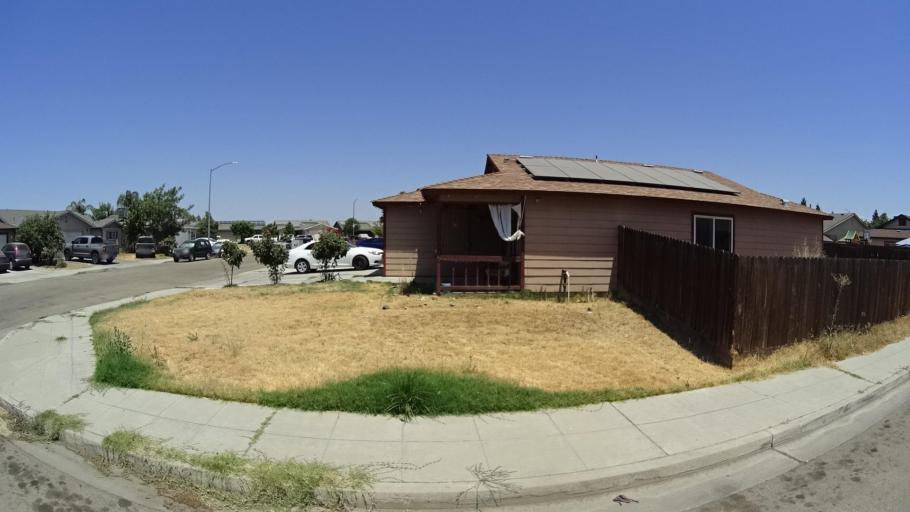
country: US
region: California
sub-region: Fresno County
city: Sunnyside
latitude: 36.7078
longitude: -119.7299
